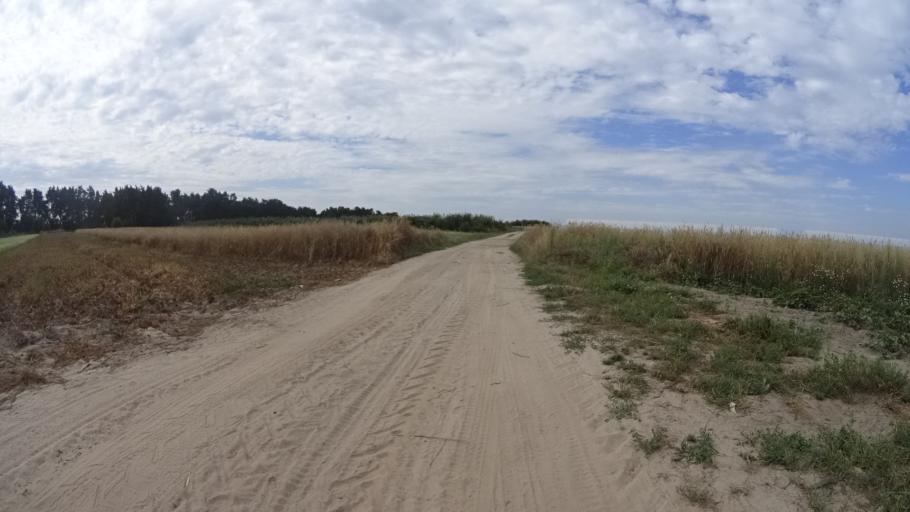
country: PL
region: Masovian Voivodeship
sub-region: Powiat bialobrzeski
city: Wysmierzyce
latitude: 51.6564
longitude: 20.8172
